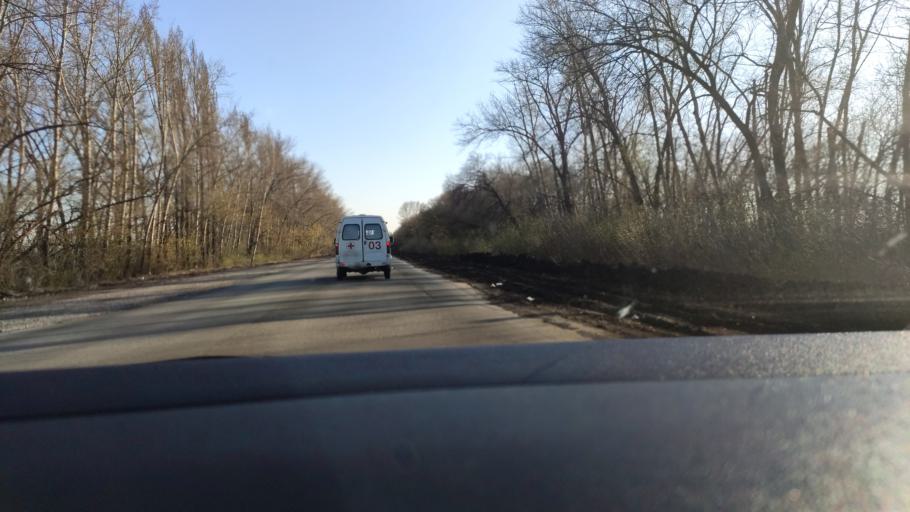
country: RU
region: Voronezj
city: Uryv-Pokrovka
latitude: 51.1695
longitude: 39.0742
